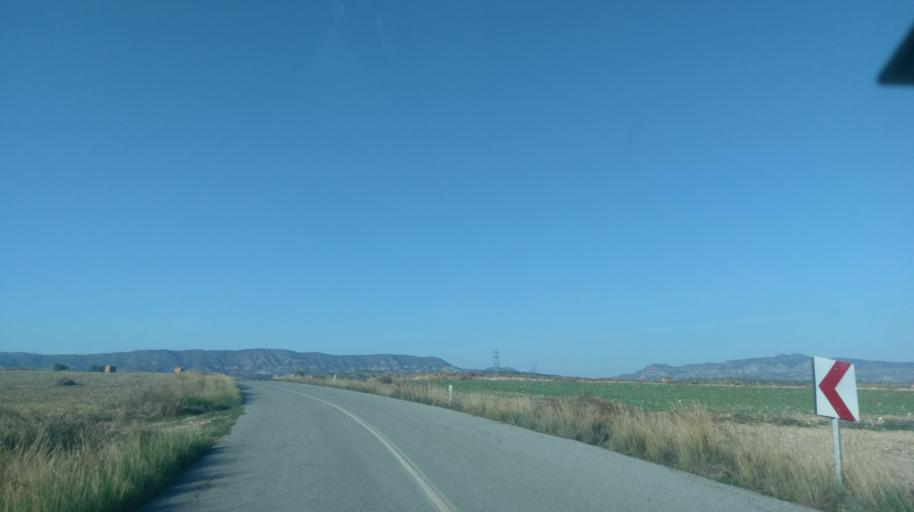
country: CY
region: Ammochostos
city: Lefkonoiko
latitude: 35.2744
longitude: 33.6879
